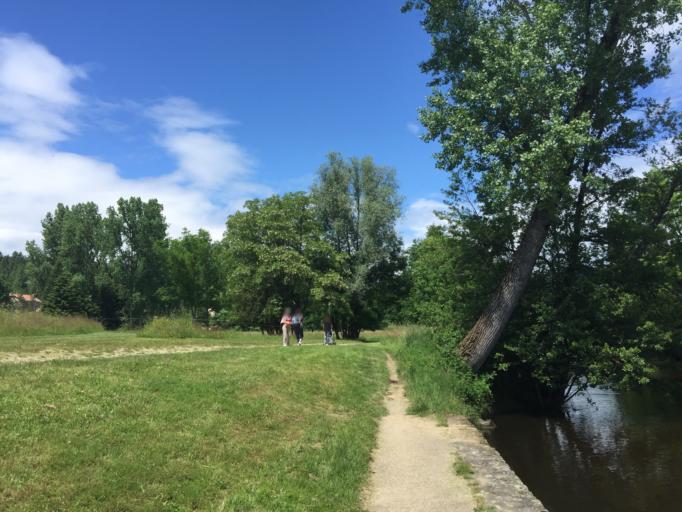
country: FR
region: Auvergne
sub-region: Departement du Puy-de-Dome
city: Ambert
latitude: 45.5442
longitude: 3.7300
